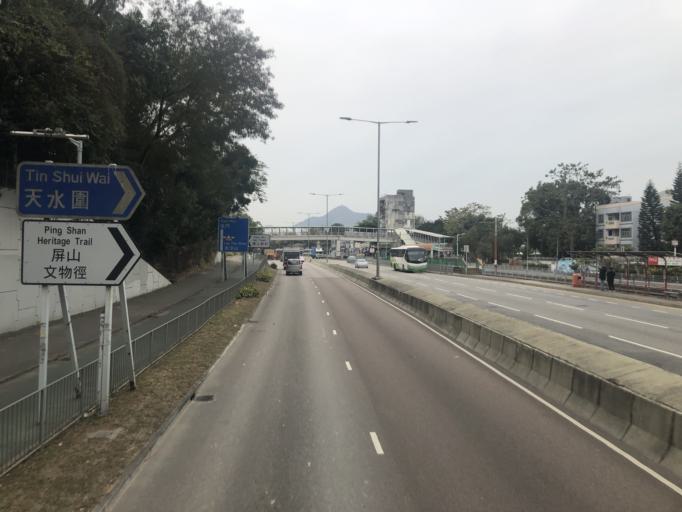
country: HK
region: Yuen Long
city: Yuen Long Kau Hui
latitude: 22.4432
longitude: 114.0133
